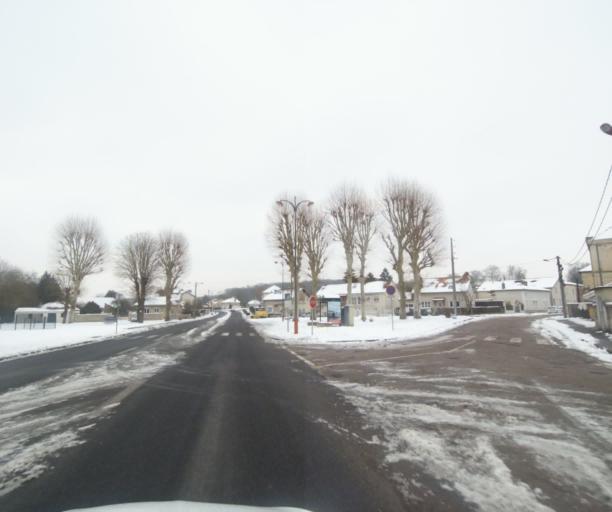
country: FR
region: Champagne-Ardenne
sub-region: Departement de la Haute-Marne
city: Saint-Dizier
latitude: 48.6172
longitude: 4.9048
